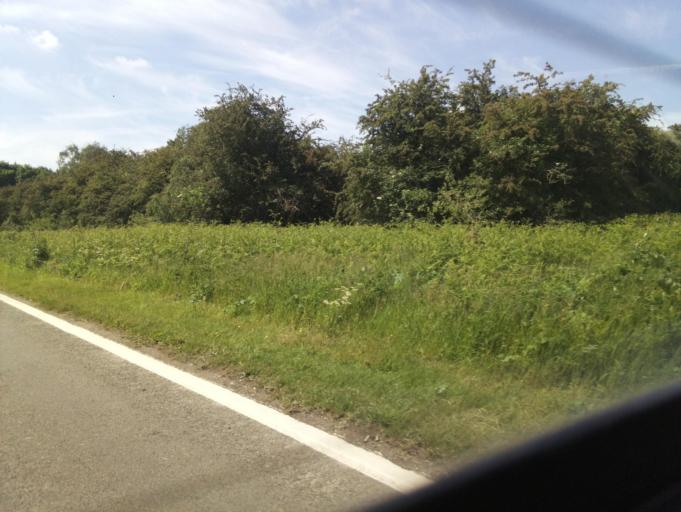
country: GB
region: England
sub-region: North Lincolnshire
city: Manton
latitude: 53.5206
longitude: -0.5800
